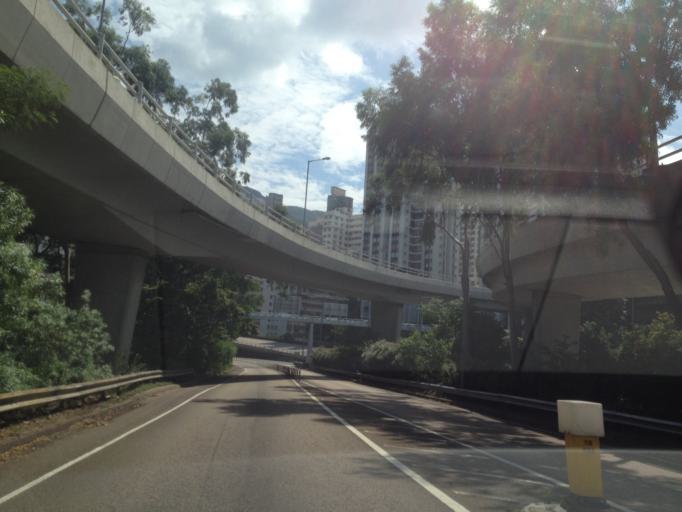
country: HK
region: Kowloon City
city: Kowloon
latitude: 22.2862
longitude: 114.2216
